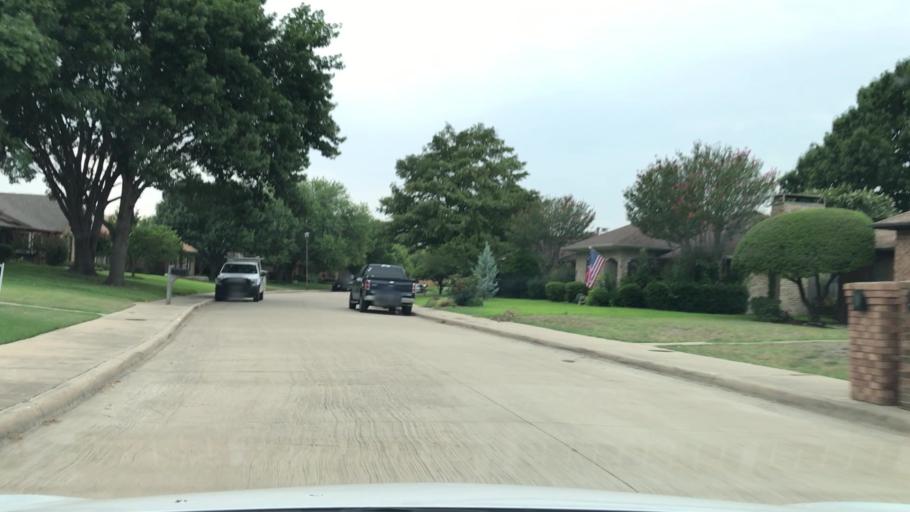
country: US
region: Texas
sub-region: Dallas County
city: Carrollton
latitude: 32.9940
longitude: -96.8688
